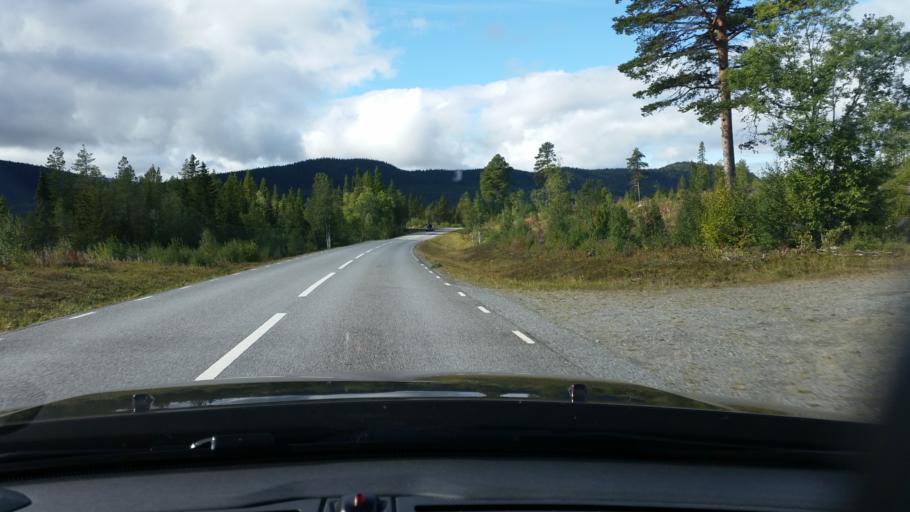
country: SE
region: Jaemtland
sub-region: Stroemsunds Kommun
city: Stroemsund
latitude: 64.3417
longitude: 14.7442
